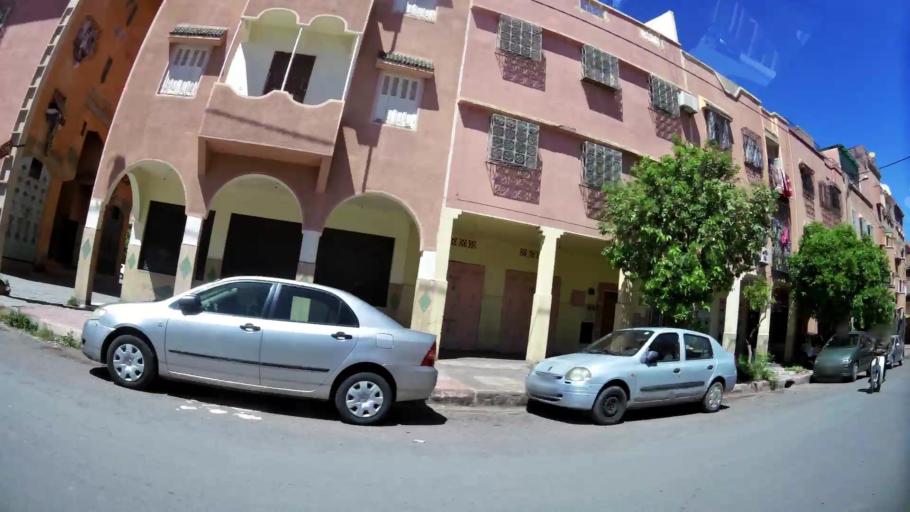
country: MA
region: Marrakech-Tensift-Al Haouz
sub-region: Marrakech
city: Marrakesh
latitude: 31.6352
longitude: -8.0637
